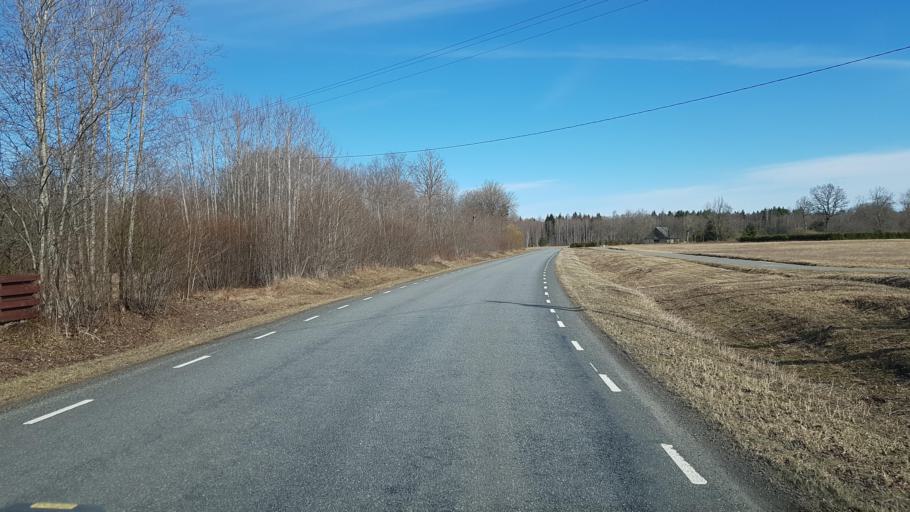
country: EE
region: Harju
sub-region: Nissi vald
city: Riisipere
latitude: 59.2374
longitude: 24.2437
